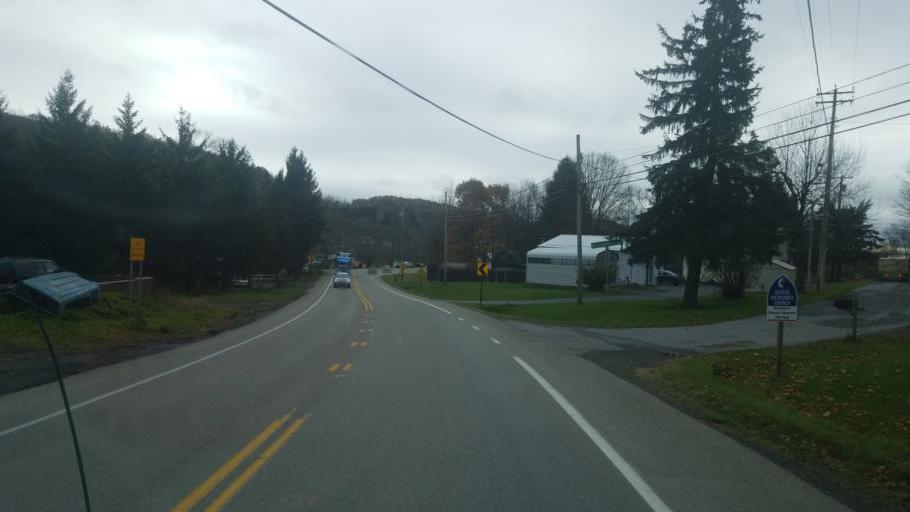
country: US
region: Pennsylvania
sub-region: Jefferson County
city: Brockway
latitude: 41.2654
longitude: -78.7212
